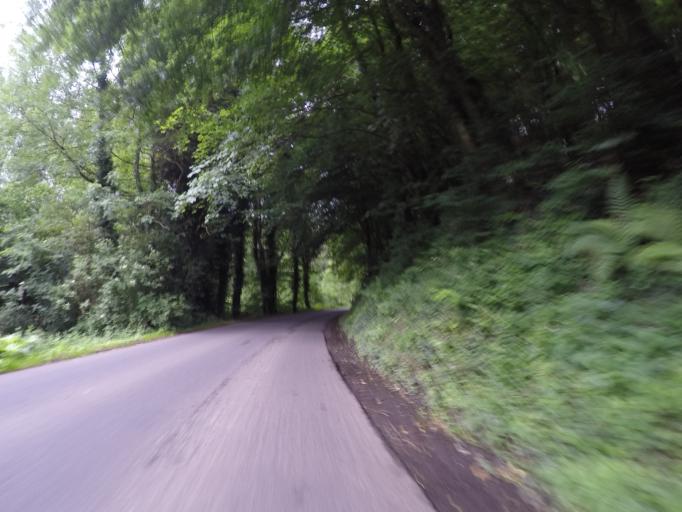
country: BE
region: Wallonia
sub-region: Province de Namur
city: Yvoir
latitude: 50.3472
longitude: 4.9351
